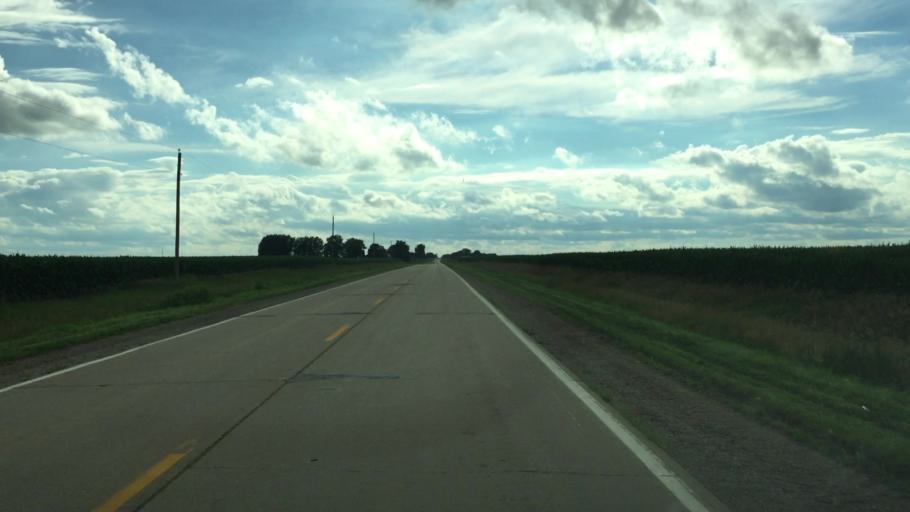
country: US
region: Iowa
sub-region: Jasper County
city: Prairie City
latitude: 41.5807
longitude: -93.1605
